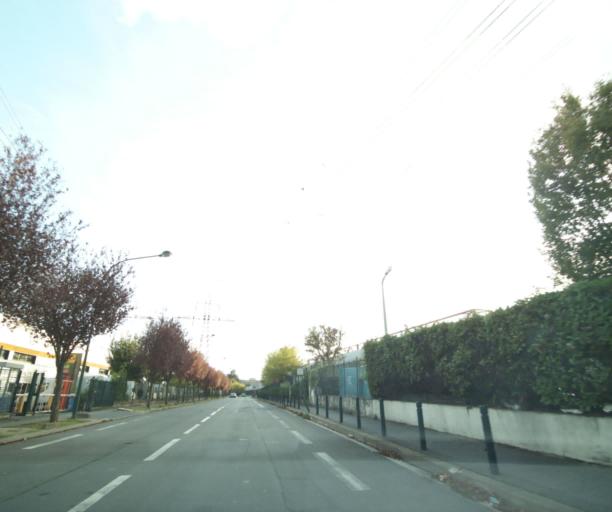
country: FR
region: Ile-de-France
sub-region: Departement des Hauts-de-Seine
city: Le Plessis-Robinson
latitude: 48.7817
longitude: 2.2478
